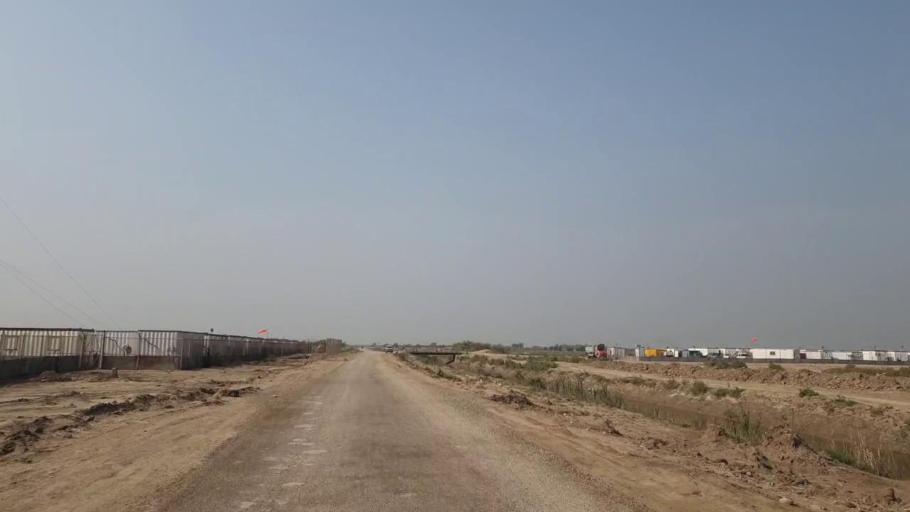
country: PK
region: Sindh
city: Tando Muhammad Khan
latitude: 24.9686
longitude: 68.5114
